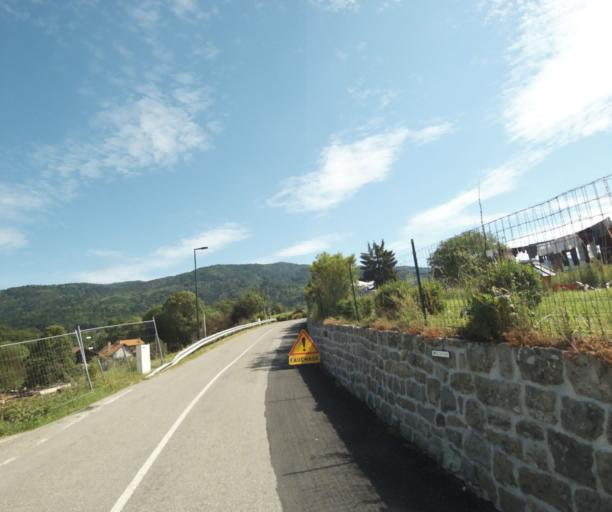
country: FR
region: Rhone-Alpes
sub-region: Departement de la Haute-Savoie
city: Bons-en-Chablais
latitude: 46.2829
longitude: 6.4155
